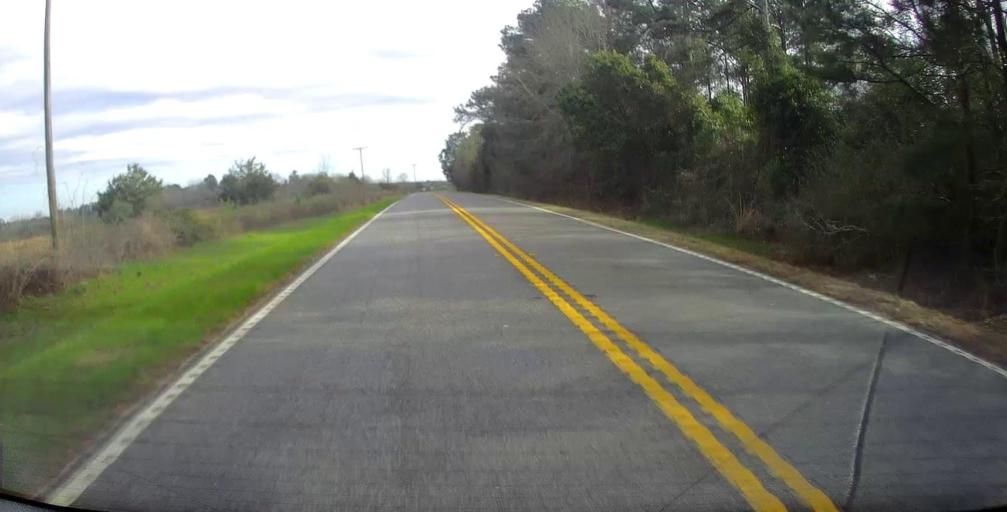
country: US
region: Georgia
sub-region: Marion County
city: Buena Vista
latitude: 32.4501
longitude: -84.4423
